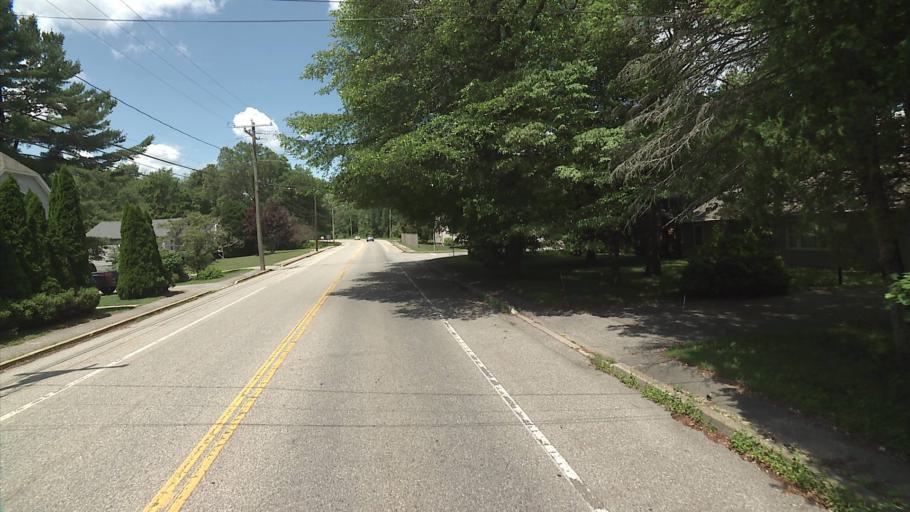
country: US
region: Connecticut
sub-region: New London County
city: Mystic
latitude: 41.3561
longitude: -71.9778
